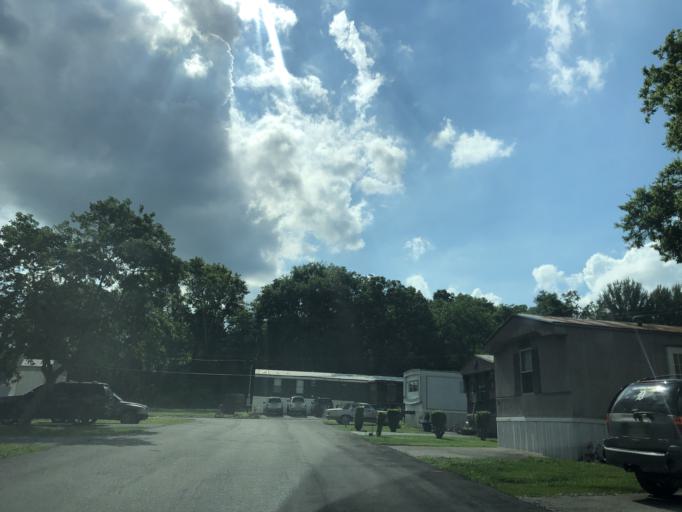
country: US
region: Tennessee
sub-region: Davidson County
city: Nashville
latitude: 36.2077
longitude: -86.7730
